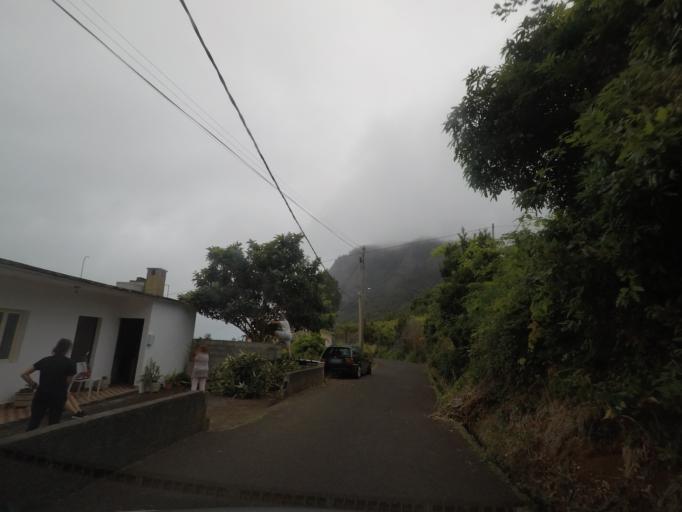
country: PT
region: Madeira
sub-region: Santana
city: Santana
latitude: 32.7687
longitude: -16.8433
